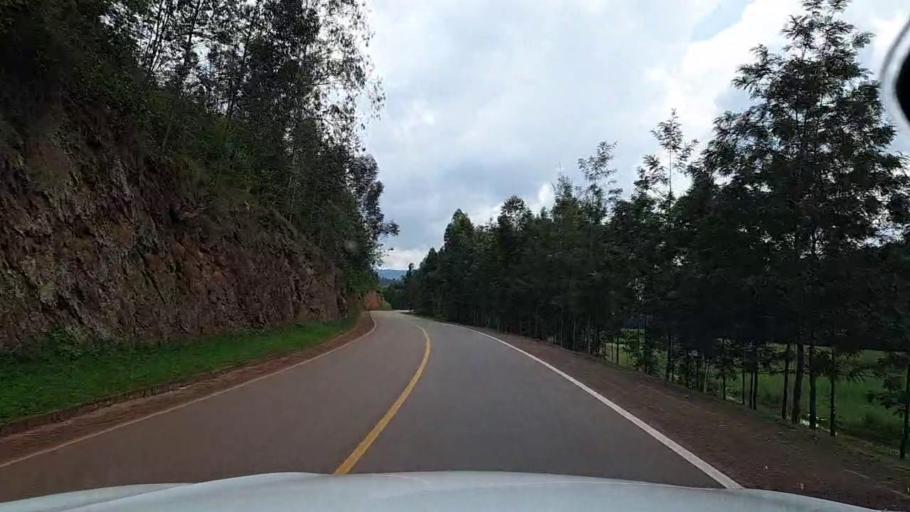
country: RW
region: Kigali
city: Kigali
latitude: -1.8175
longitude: 30.1173
